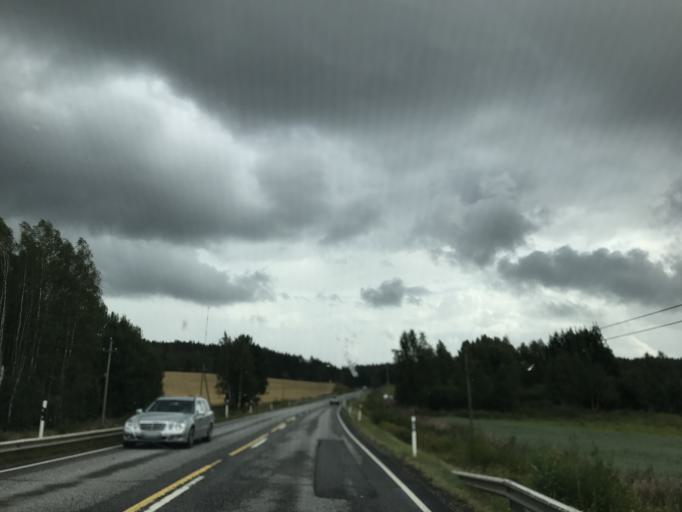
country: FI
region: Varsinais-Suomi
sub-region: Salo
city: Pernioe
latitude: 60.0902
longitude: 23.2266
